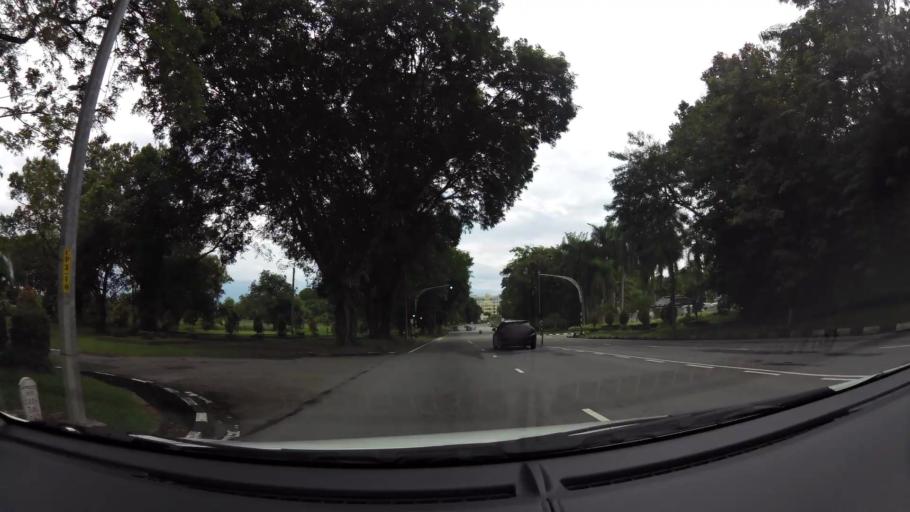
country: BN
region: Brunei and Muara
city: Bandar Seri Begawan
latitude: 4.9094
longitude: 114.9315
